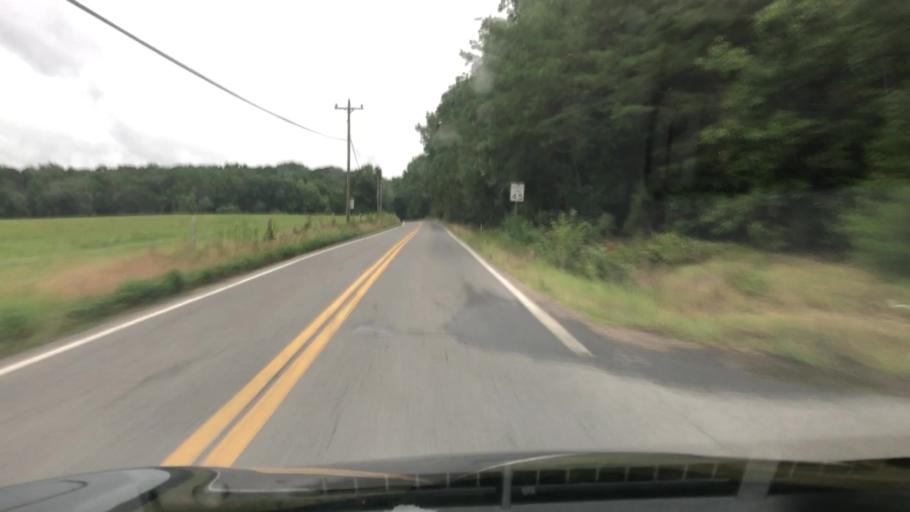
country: US
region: Virginia
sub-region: Fauquier County
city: Bealeton
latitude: 38.5177
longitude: -77.6082
